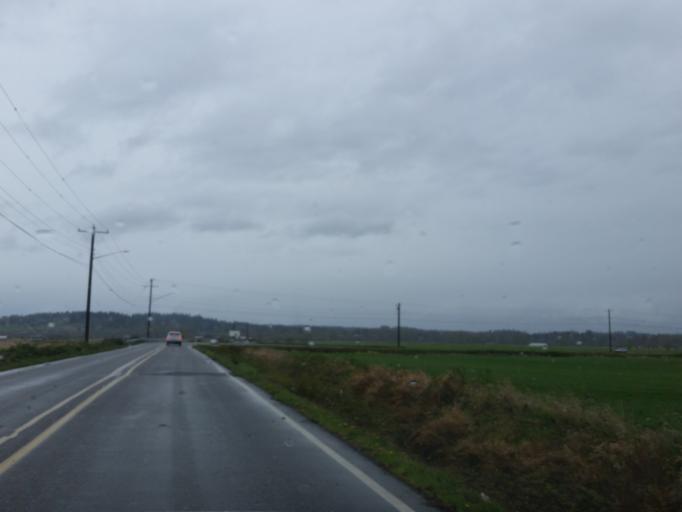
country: US
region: Washington
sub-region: Snohomish County
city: Silver Firs
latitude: 47.8977
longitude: -122.1372
